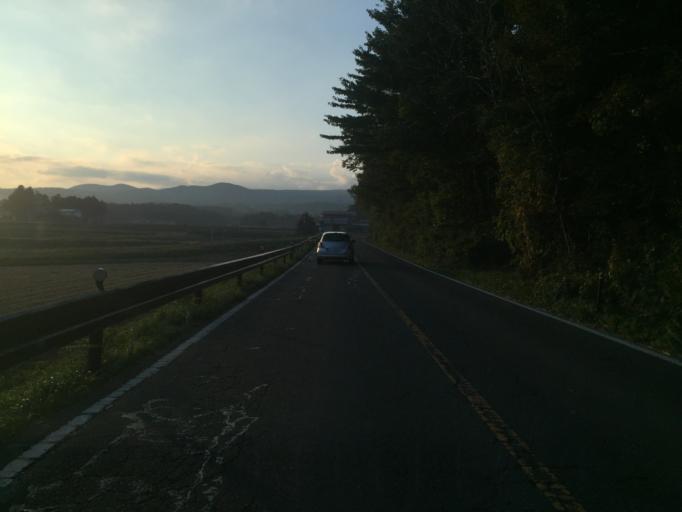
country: JP
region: Fukushima
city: Motomiya
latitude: 37.5513
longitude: 140.3628
